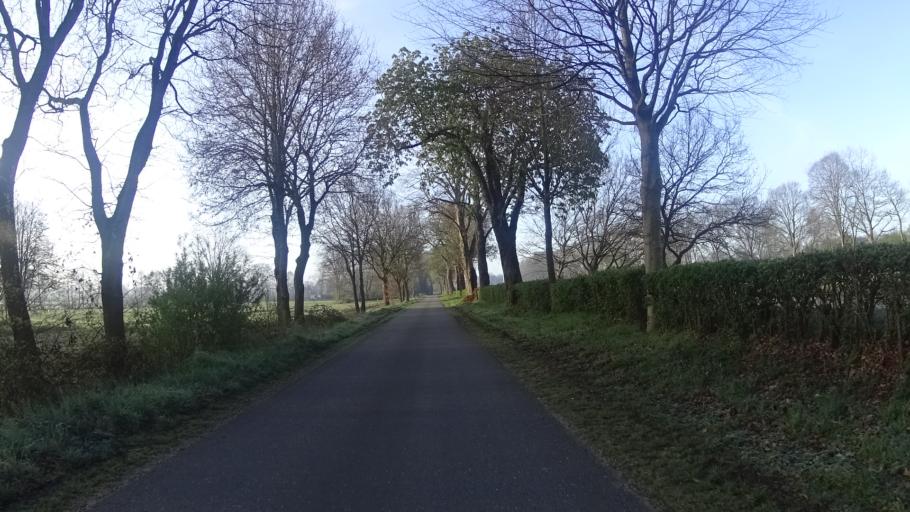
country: DE
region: Lower Saxony
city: Fresenburg
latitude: 52.8910
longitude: 7.3138
